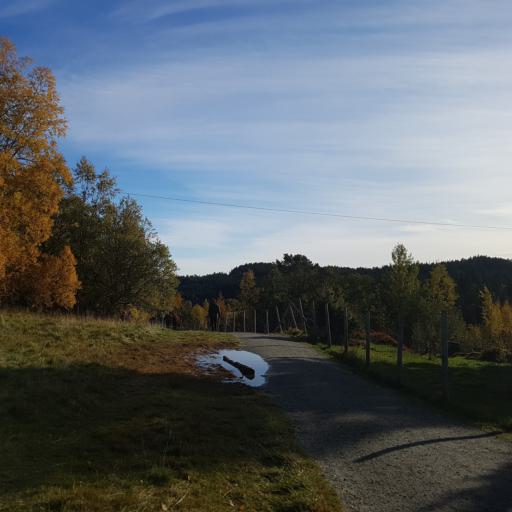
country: NO
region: Sor-Trondelag
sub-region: Trondheim
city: Trondheim
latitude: 63.4216
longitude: 10.3066
